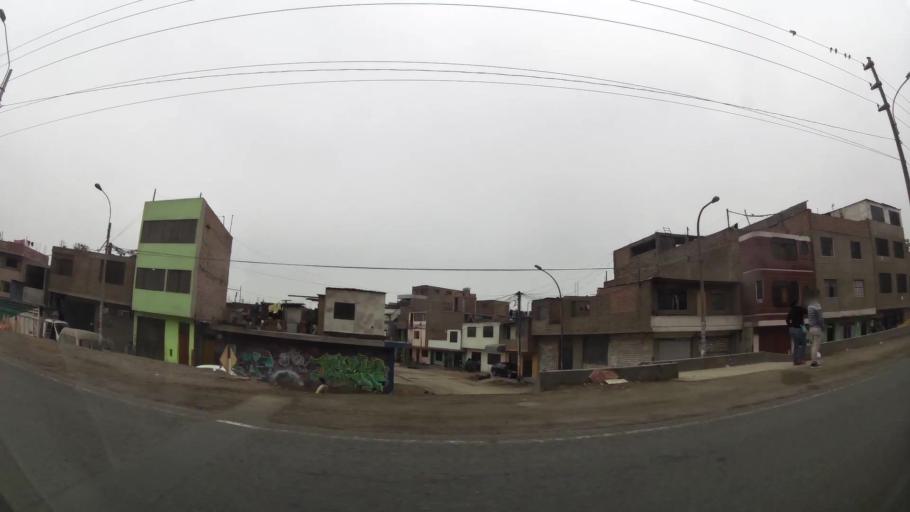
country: PE
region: Lima
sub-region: Lima
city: Urb. Santo Domingo
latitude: -11.9092
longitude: -77.0365
